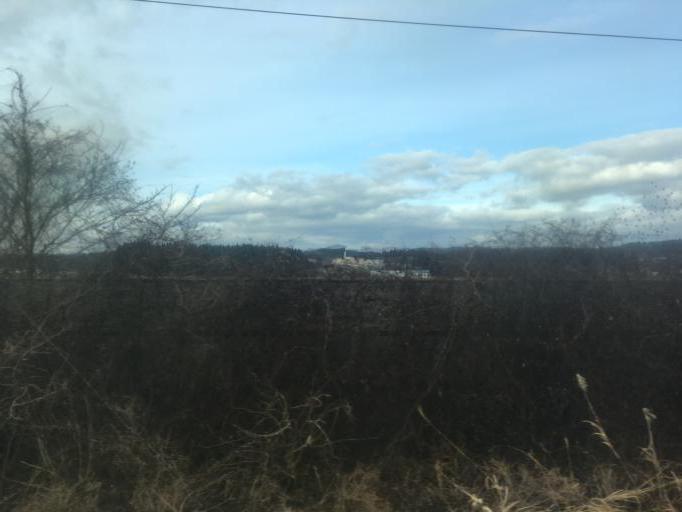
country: JP
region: Akita
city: Takanosu
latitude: 40.2493
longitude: 140.3959
